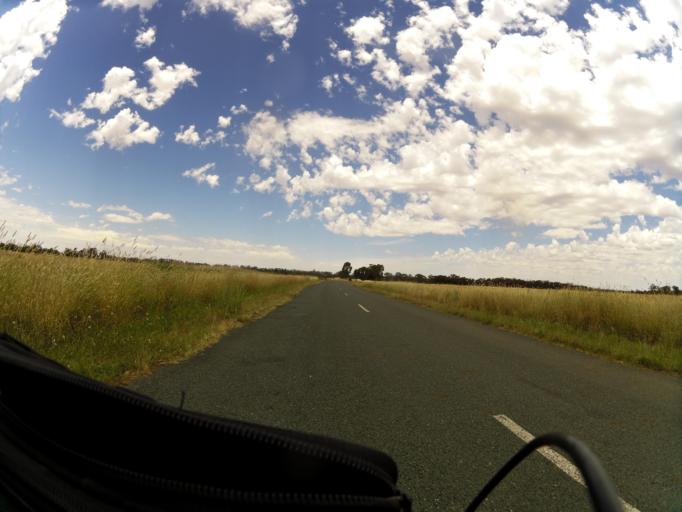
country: AU
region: Victoria
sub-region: Greater Shepparton
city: Shepparton
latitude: -36.6741
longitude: 145.1967
